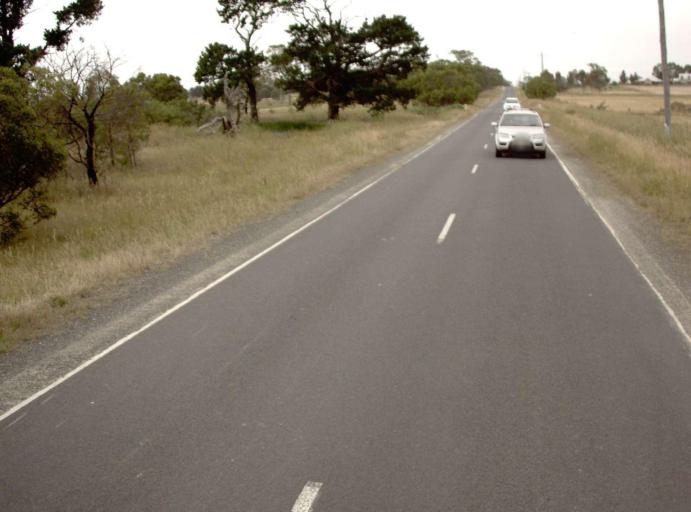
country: AU
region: Victoria
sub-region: Wellington
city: Heyfield
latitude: -38.0340
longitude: 146.7663
